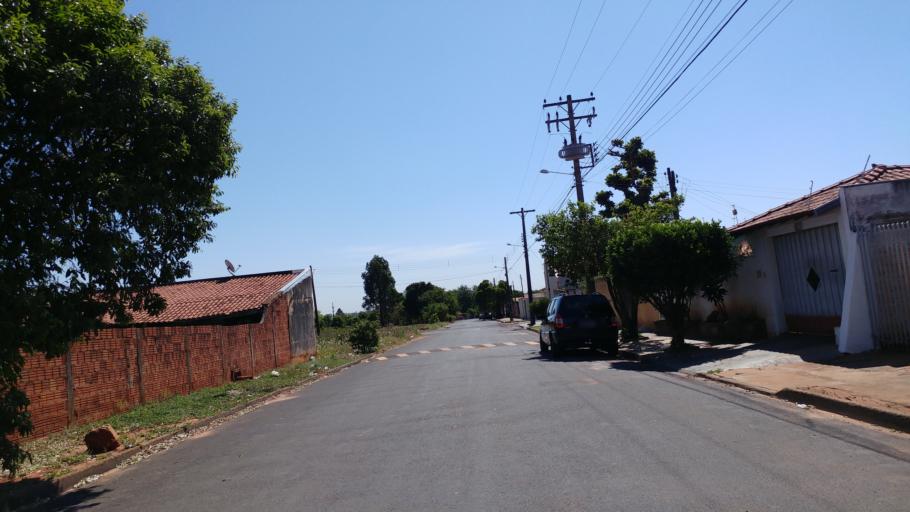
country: BR
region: Sao Paulo
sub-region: Paraguacu Paulista
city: Paraguacu Paulista
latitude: -22.4131
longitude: -50.5928
